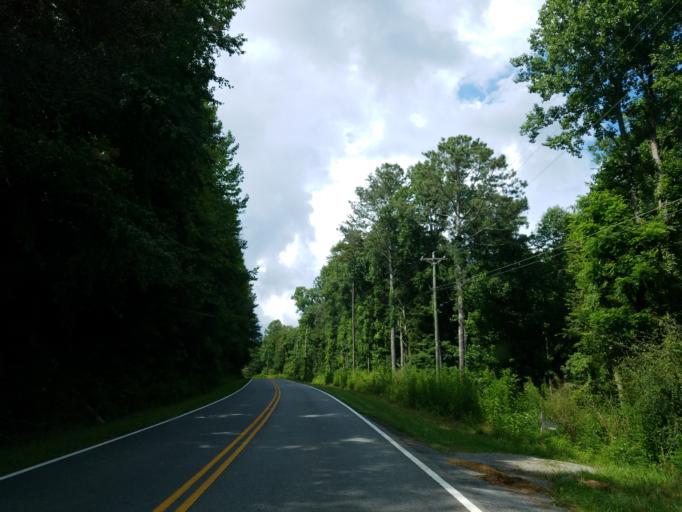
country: US
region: Georgia
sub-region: Gilmer County
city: Ellijay
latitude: 34.6638
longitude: -84.3825
